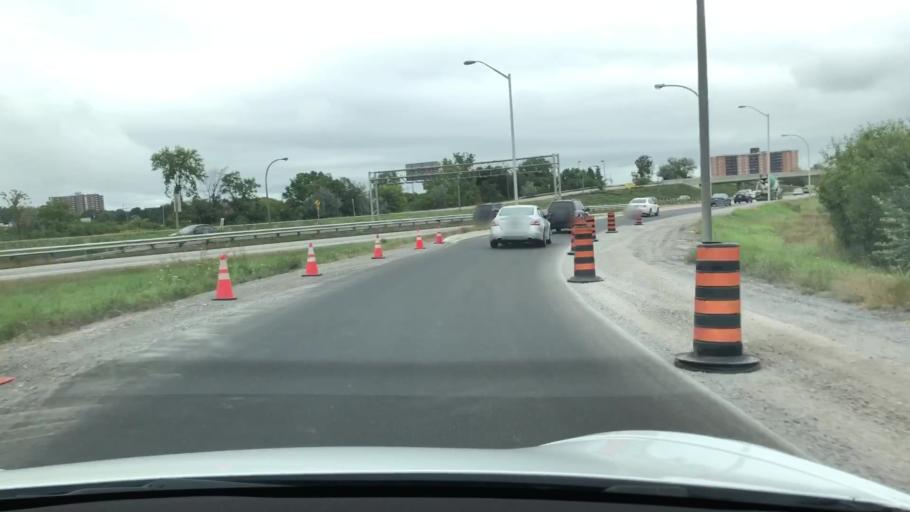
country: CA
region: Ontario
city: Ottawa
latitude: 45.4332
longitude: -75.6022
